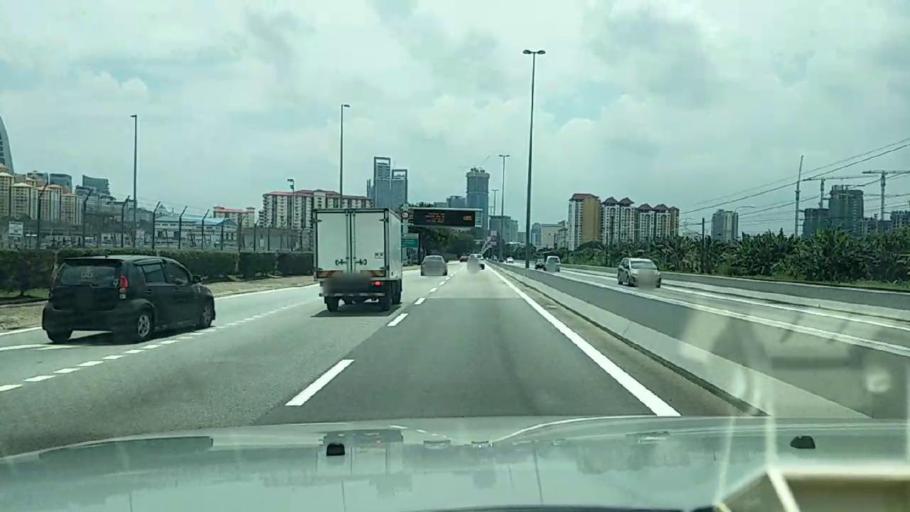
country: MY
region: Kuala Lumpur
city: Kuala Lumpur
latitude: 3.0997
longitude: 101.6709
